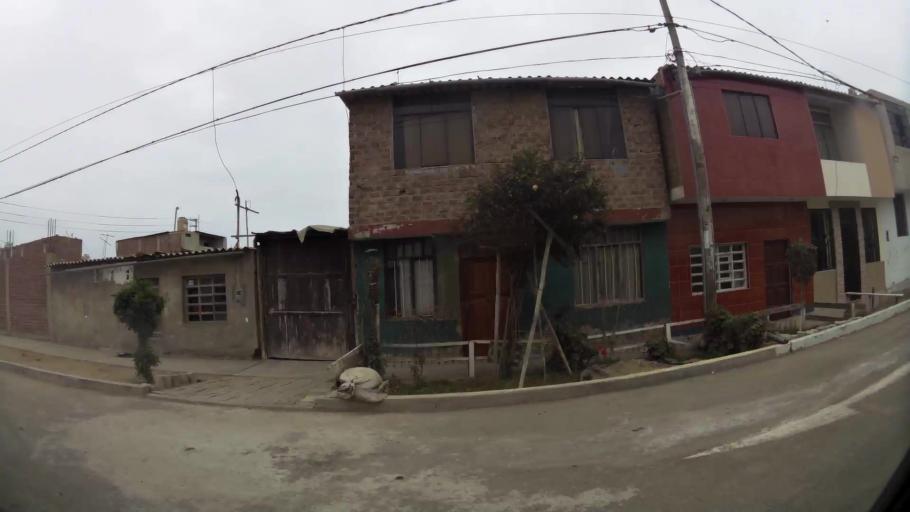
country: PE
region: La Libertad
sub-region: Provincia de Trujillo
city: Buenos Aires
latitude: -8.1476
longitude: -79.0461
